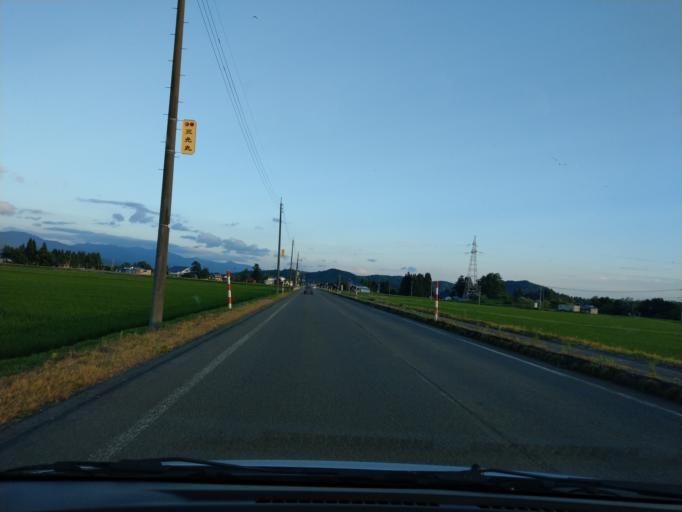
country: JP
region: Akita
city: Kakunodatemachi
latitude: 39.6311
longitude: 140.5704
